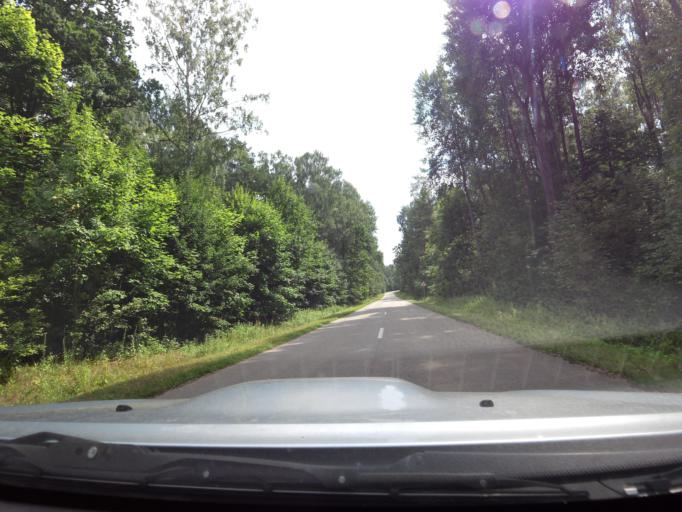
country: RU
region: Kaliningrad
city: Neman
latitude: 55.0880
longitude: 22.0386
